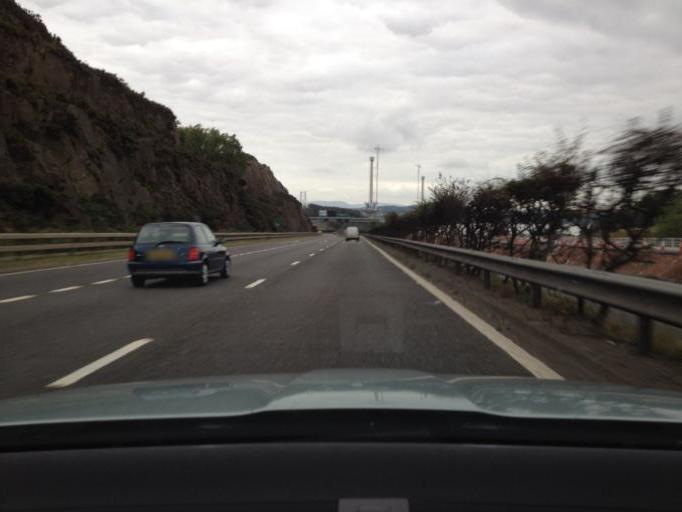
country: GB
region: Scotland
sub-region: Fife
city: Inverkeithing
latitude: 56.0267
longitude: -3.4079
